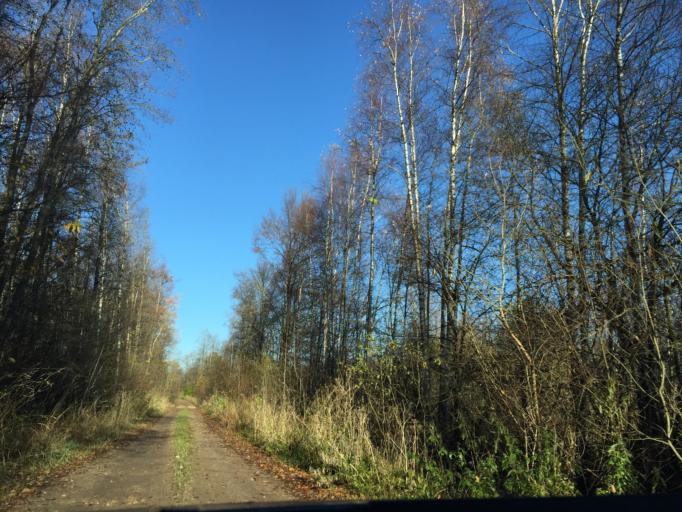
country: LV
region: Aizkraukles Rajons
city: Aizkraukle
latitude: 56.7199
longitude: 25.2996
